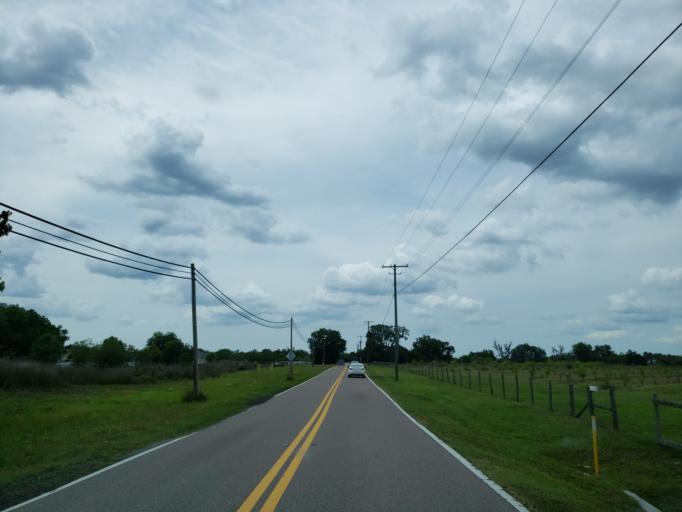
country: US
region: Florida
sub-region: Hillsborough County
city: Keystone
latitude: 28.1156
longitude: -82.6063
